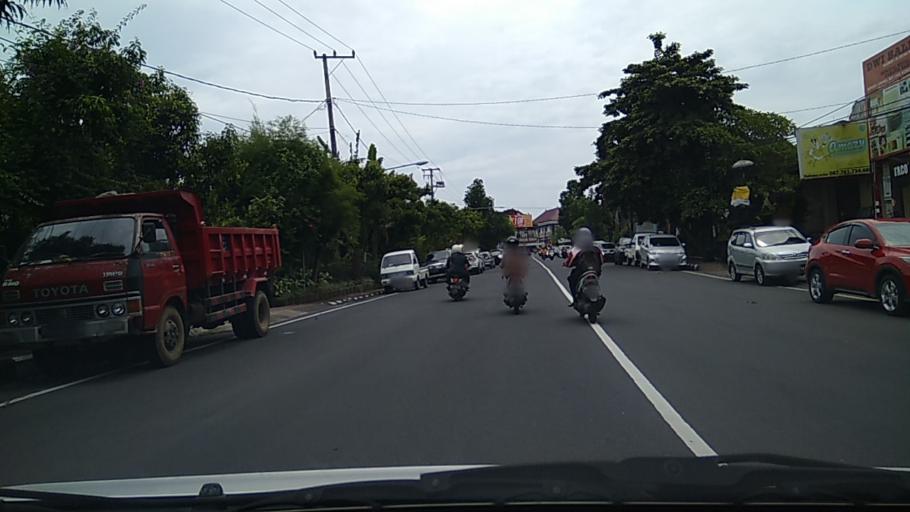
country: ID
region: Bali
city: Banjar Pesalakan
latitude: -8.5356
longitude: 115.3212
